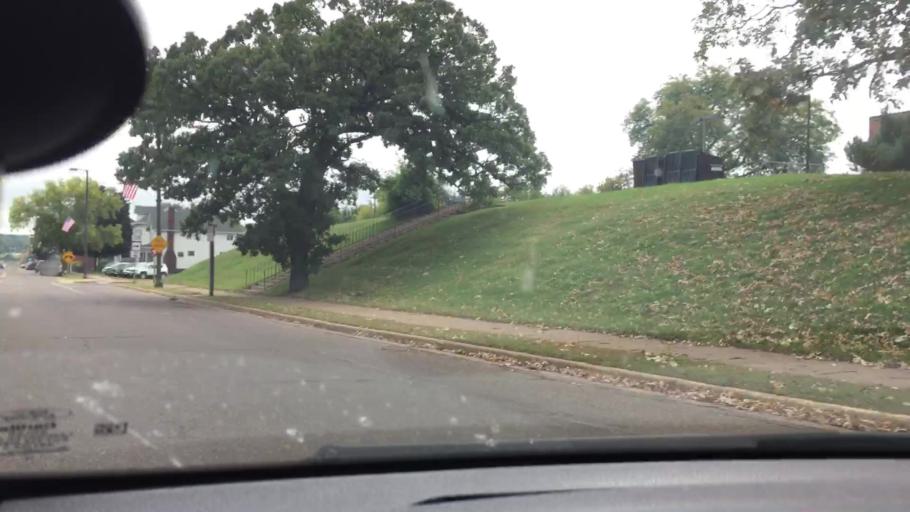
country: US
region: Wisconsin
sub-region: Chippewa County
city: Chippewa Falls
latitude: 44.9411
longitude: -91.3982
